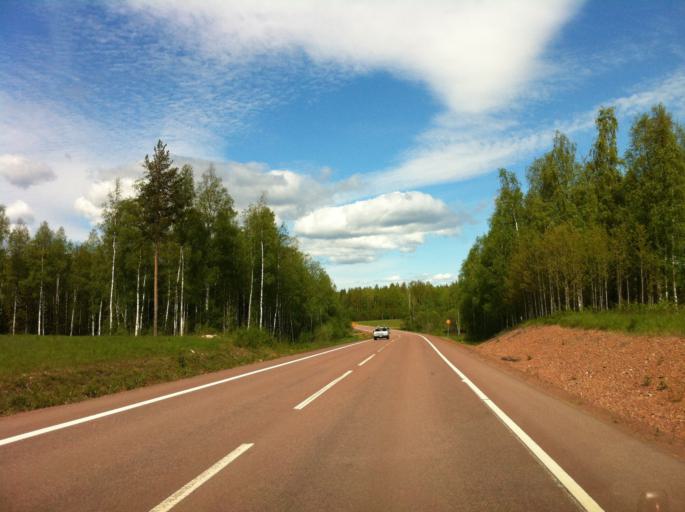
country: SE
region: Dalarna
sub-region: Mora Kommun
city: Mora
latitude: 60.9178
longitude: 14.5984
